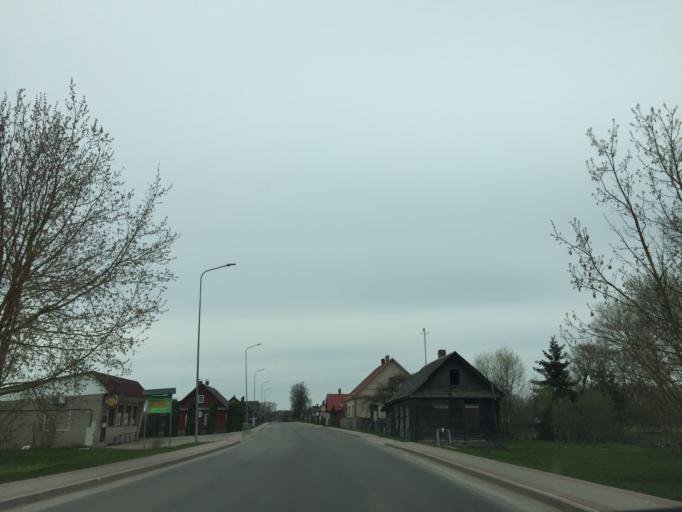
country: LV
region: Ludzas Rajons
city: Ludza
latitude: 56.5560
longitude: 27.7258
